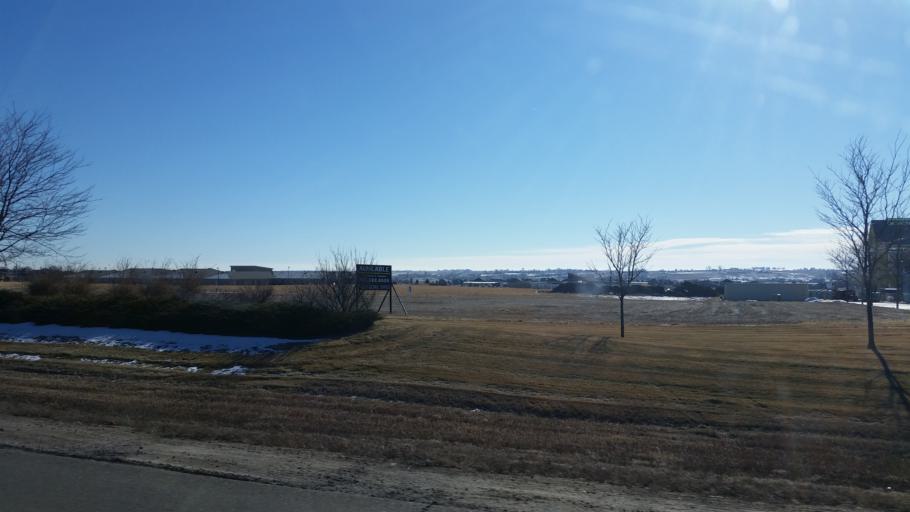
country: US
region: Colorado
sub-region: Weld County
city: Johnstown
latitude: 40.4071
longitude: -104.9785
